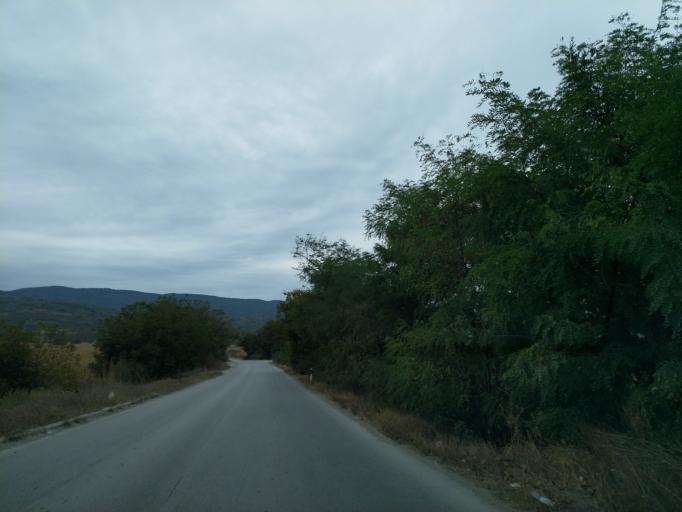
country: RS
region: Central Serbia
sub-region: Pomoravski Okrug
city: Paracin
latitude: 43.8288
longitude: 21.3430
